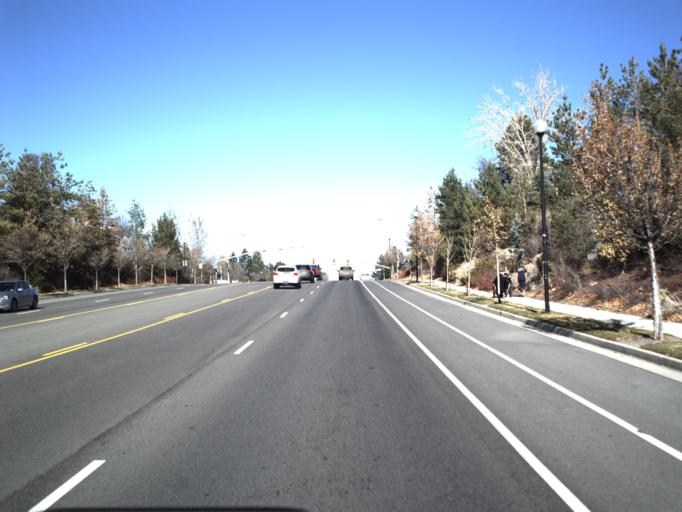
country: US
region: Utah
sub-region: Salt Lake County
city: Little Cottonwood Creek Valley
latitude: 40.5880
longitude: -111.8341
